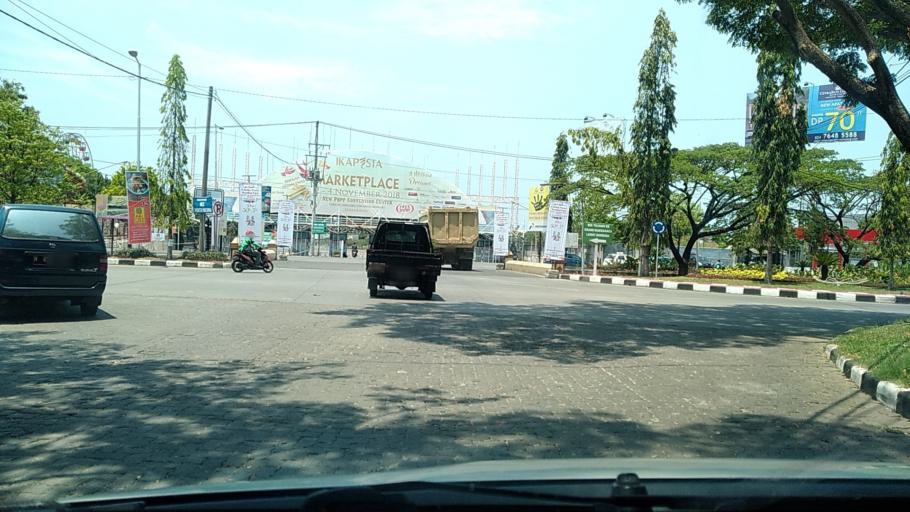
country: ID
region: Central Java
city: Semarang
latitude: -6.9629
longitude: 110.3906
